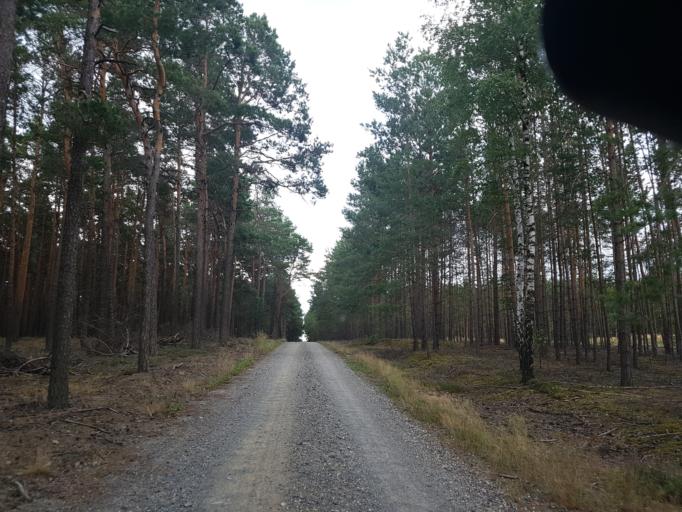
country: DE
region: Brandenburg
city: Sallgast
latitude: 51.6242
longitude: 13.8053
